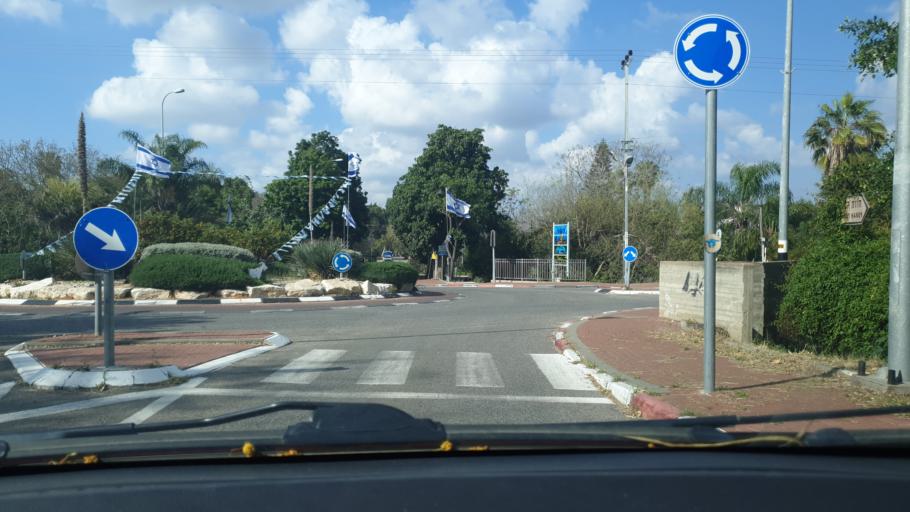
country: IL
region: Central District
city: Bet Yizhaq
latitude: 32.3435
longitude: 34.9150
